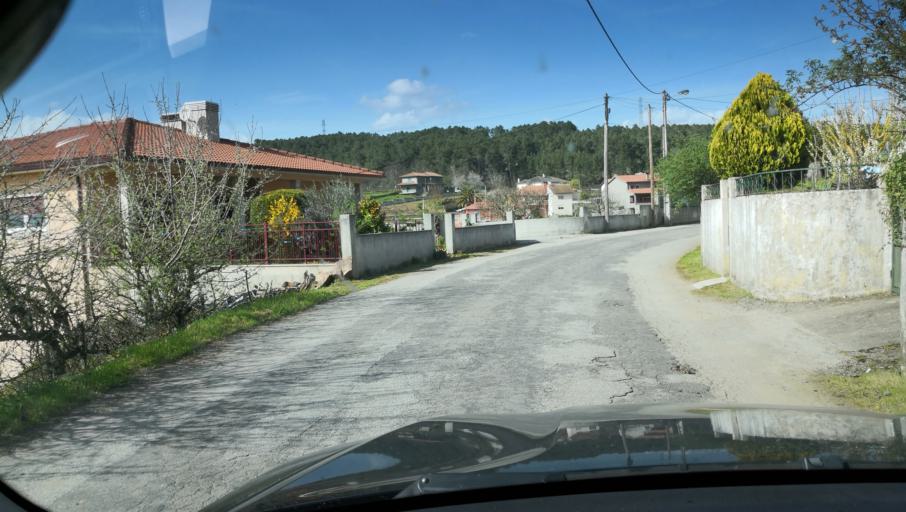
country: PT
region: Vila Real
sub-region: Sabrosa
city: Vilela
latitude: 41.2681
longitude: -7.6588
